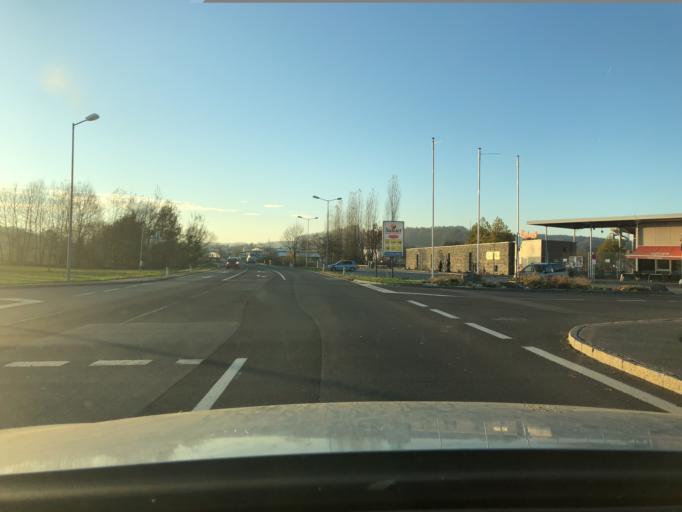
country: AT
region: Styria
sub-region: Politischer Bezirk Weiz
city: Sinabelkirchen
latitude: 47.1012
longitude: 15.8250
